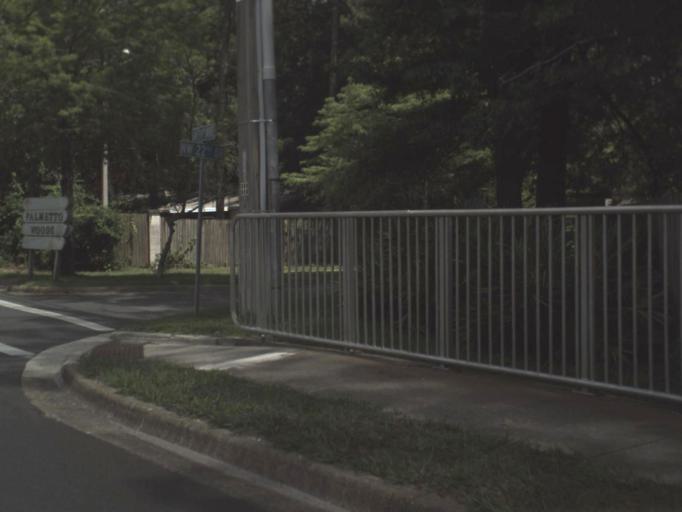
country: US
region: Florida
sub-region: Alachua County
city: Gainesville
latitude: 29.6884
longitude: -82.3545
